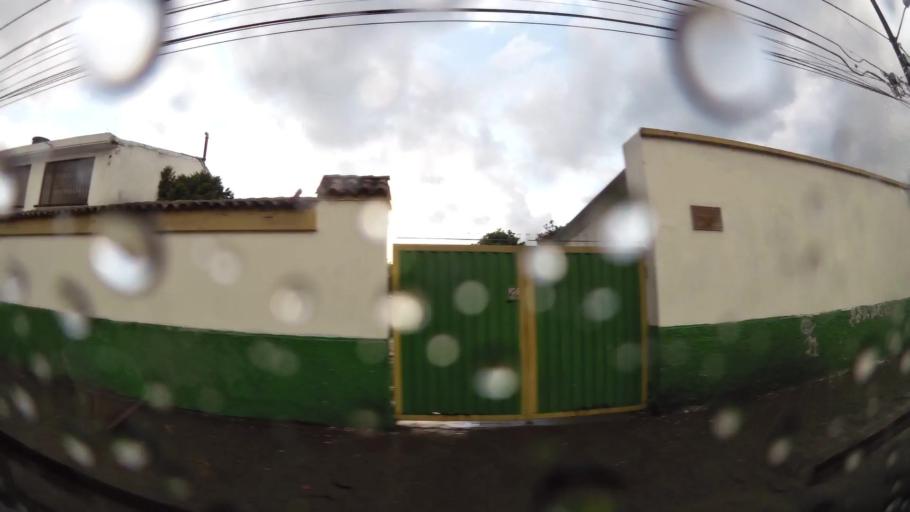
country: CO
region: Cundinamarca
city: Chia
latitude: 4.8570
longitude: -74.0586
